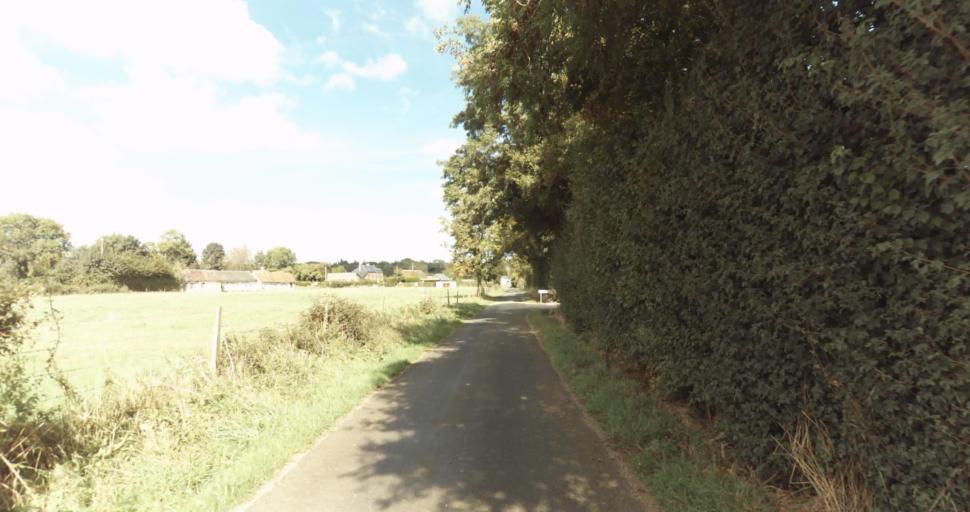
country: FR
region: Lower Normandy
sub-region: Departement du Calvados
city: Orbec
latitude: 48.9234
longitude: 0.3790
